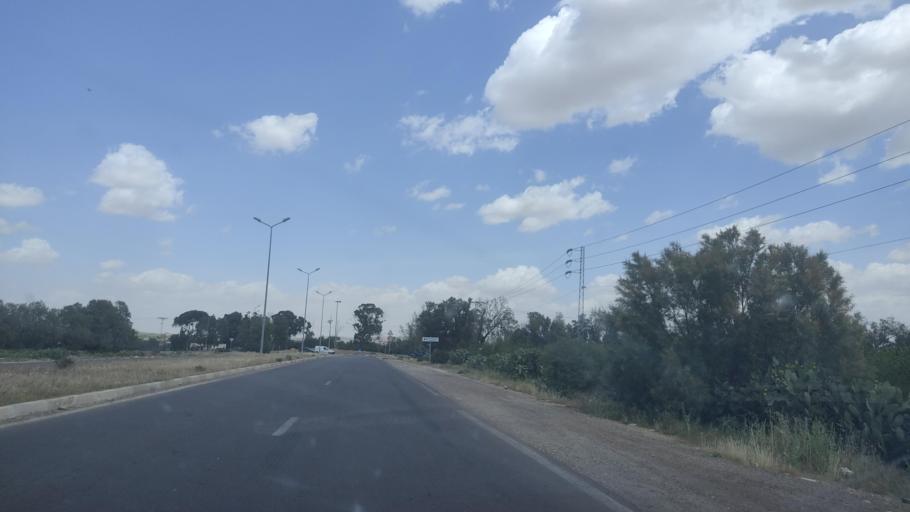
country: TN
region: Al Qasrayn
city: Kasserine
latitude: 35.1972
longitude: 8.8739
